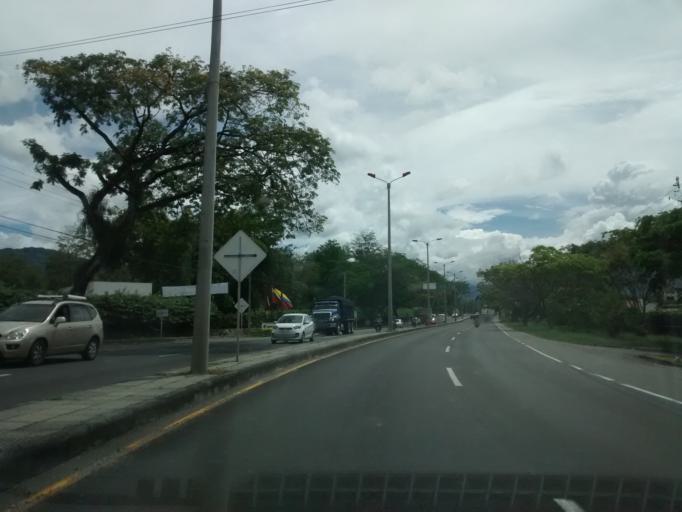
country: CO
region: Tolima
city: Ibague
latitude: 4.4046
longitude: -75.1620
